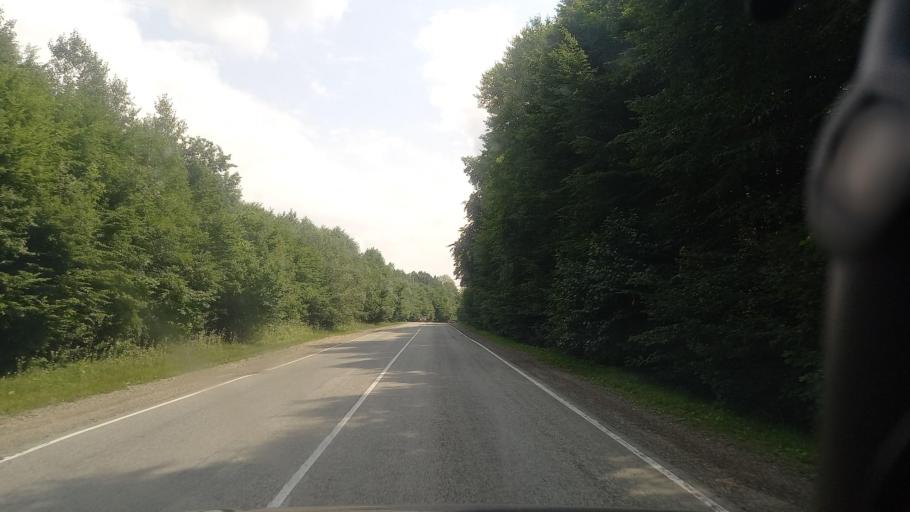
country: RU
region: Karachayevo-Cherkesiya
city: Kurdzhinovo
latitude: 44.0381
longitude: 40.9001
